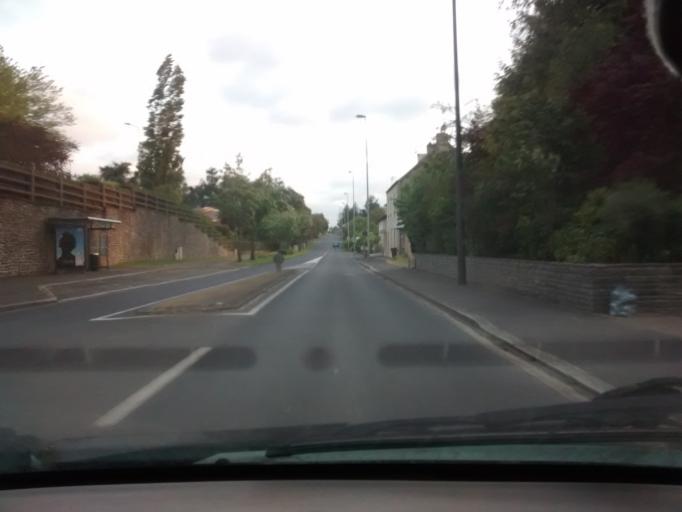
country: FR
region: Lower Normandy
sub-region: Departement de la Manche
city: Agneaux
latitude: 49.1066
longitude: -1.1090
